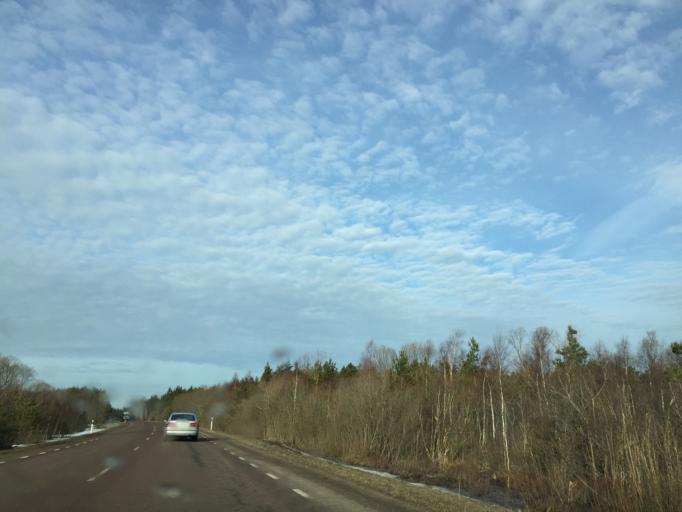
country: EE
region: Saare
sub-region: Kuressaare linn
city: Kuressaare
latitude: 58.2840
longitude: 22.4215
